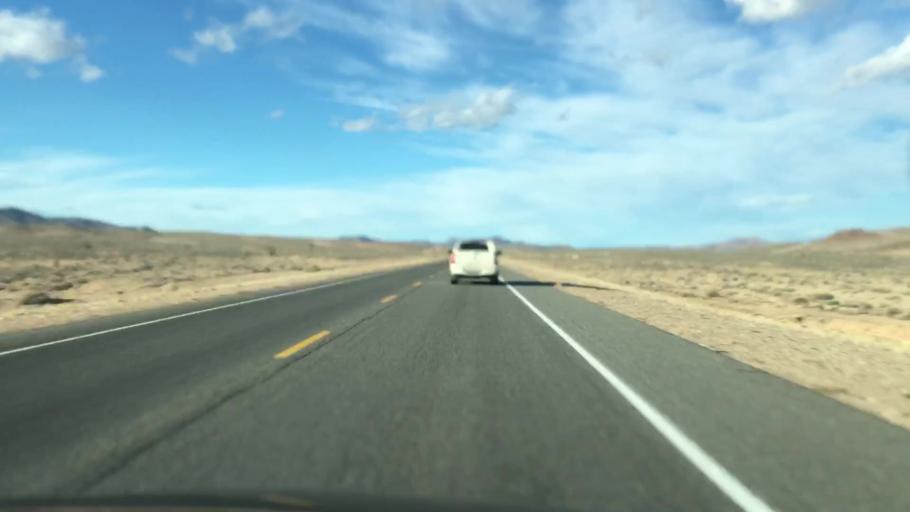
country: US
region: Nevada
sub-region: Esmeralda County
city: Goldfield
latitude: 37.5515
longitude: -117.1976
